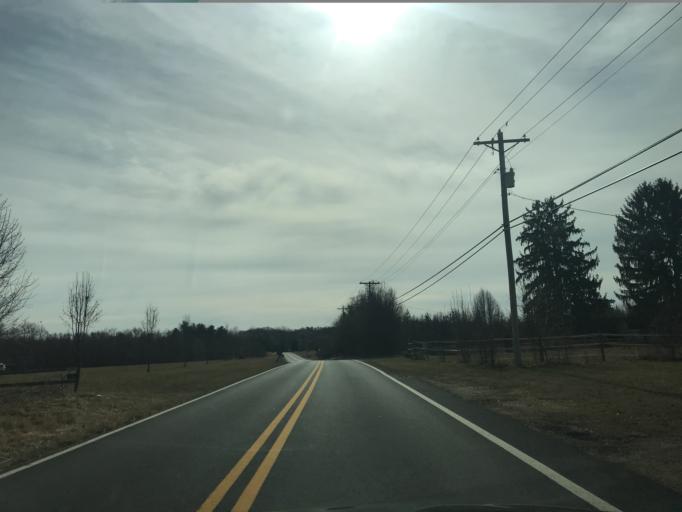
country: US
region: Virginia
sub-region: Prince William County
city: Cherry Hill
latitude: 38.5108
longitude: -77.2300
